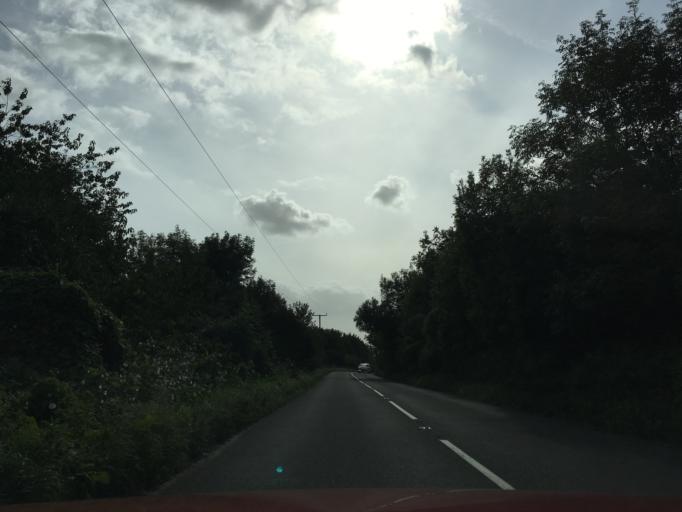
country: GB
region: England
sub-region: Gloucestershire
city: Wotton-under-Edge
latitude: 51.6561
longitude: -2.3311
